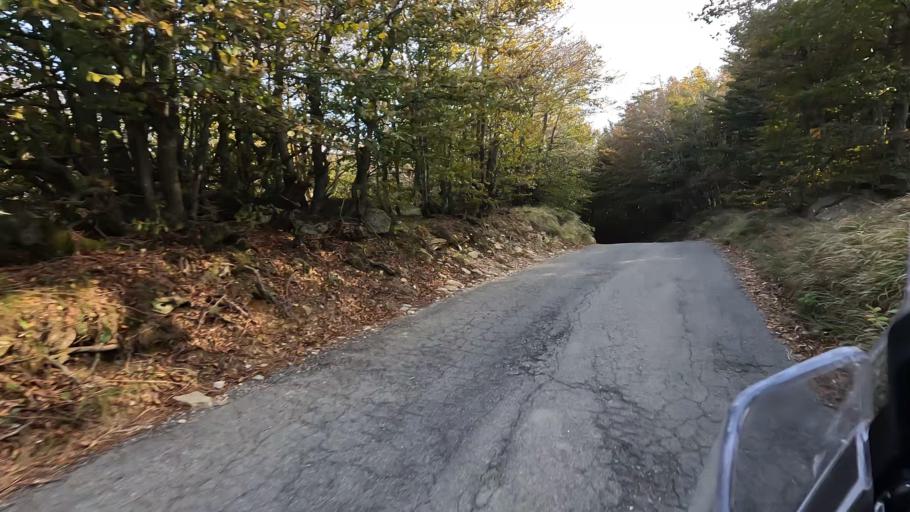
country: IT
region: Liguria
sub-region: Provincia di Genova
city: Sciarborasca
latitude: 44.4314
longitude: 8.5865
